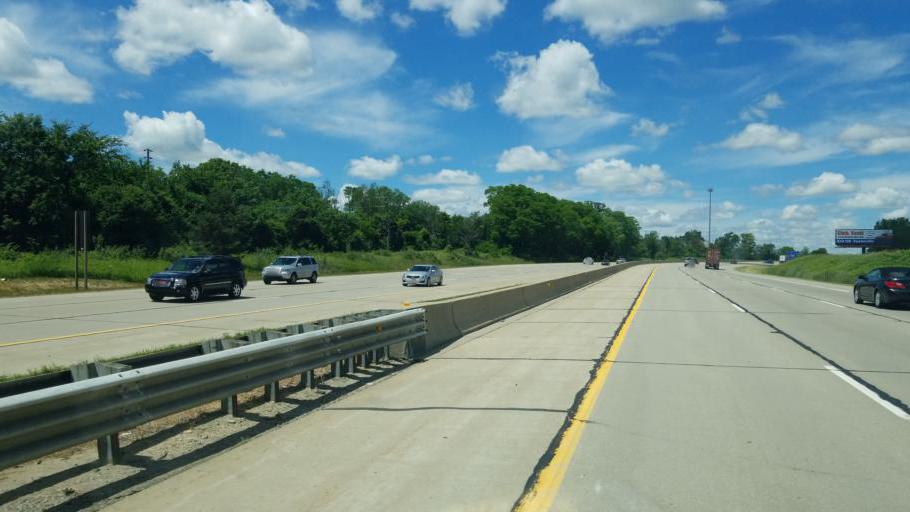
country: US
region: Michigan
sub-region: Livingston County
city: Howell
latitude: 42.5849
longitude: -83.9218
